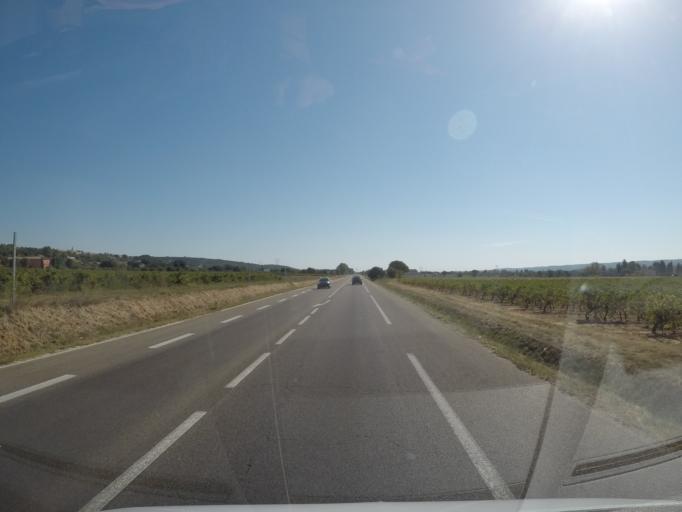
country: FR
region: Languedoc-Roussillon
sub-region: Departement du Gard
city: Uzes
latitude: 43.9900
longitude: 4.4374
